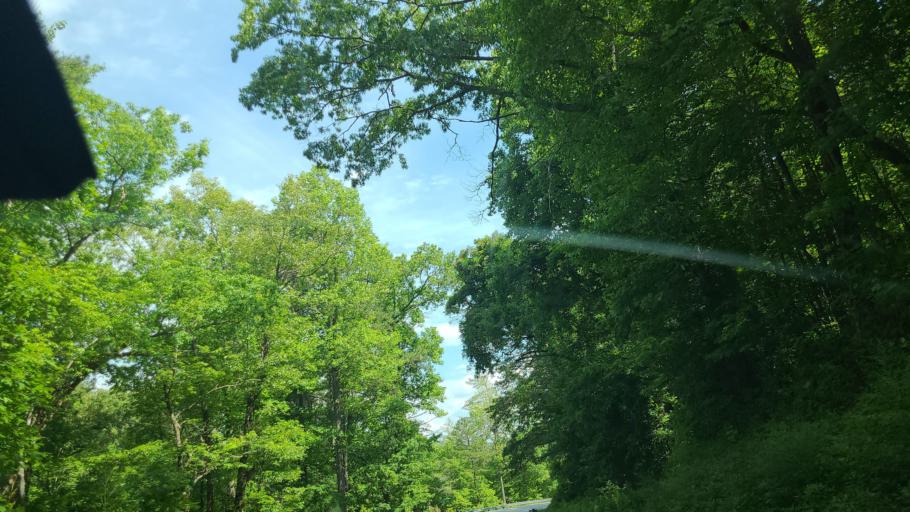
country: US
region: South Carolina
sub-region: Oconee County
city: Walhalla
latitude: 34.9007
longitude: -83.1824
